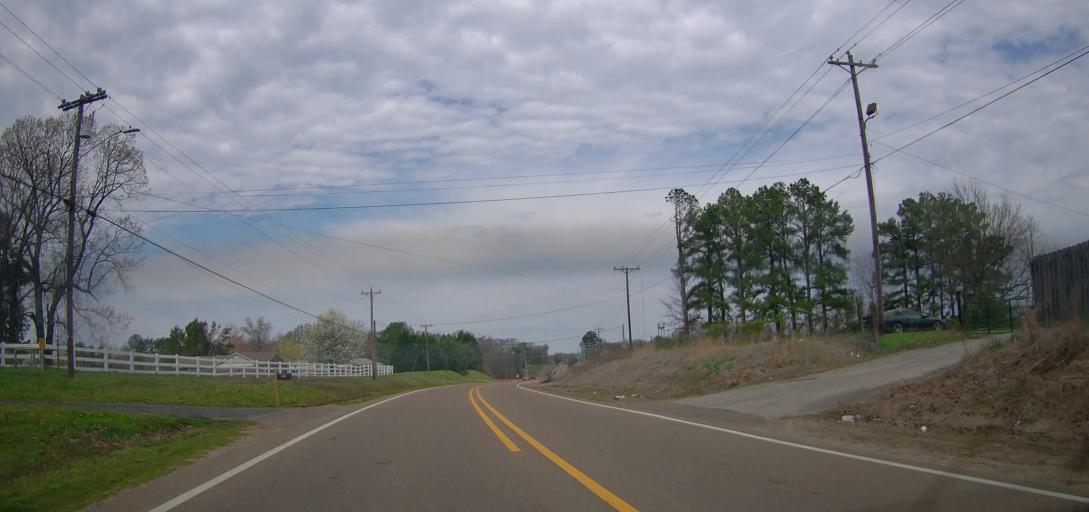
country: US
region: Mississippi
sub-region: De Soto County
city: Olive Branch
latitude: 34.9810
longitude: -89.8563
